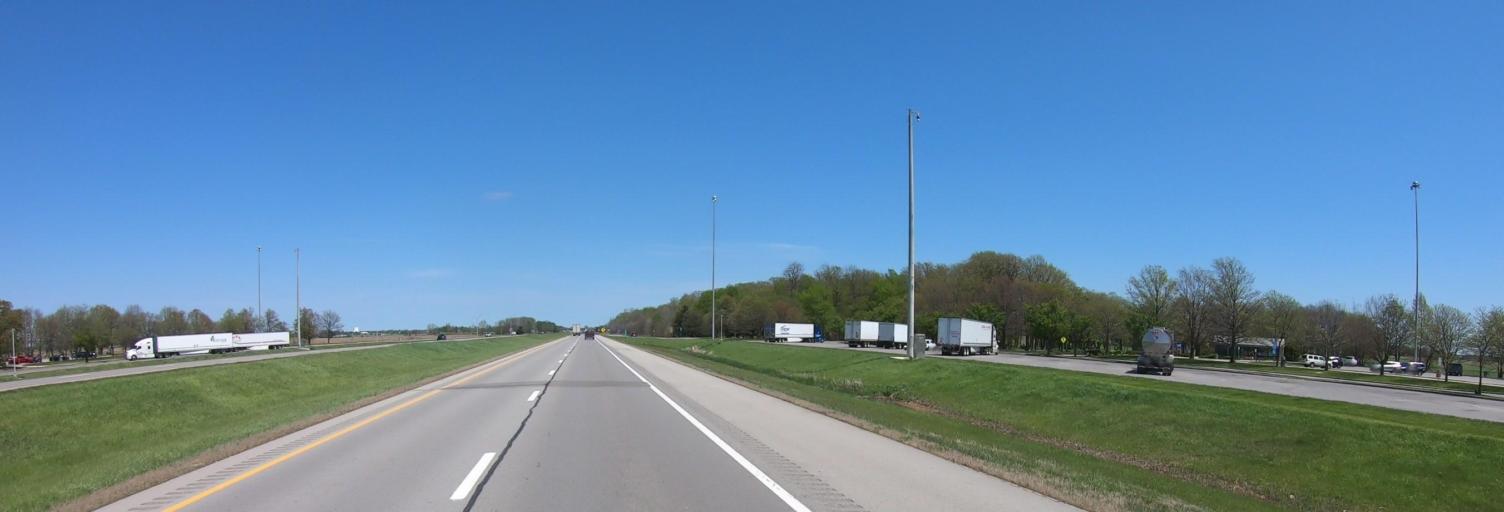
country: US
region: Ohio
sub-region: Hancock County
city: Findlay
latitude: 40.9855
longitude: -83.7140
